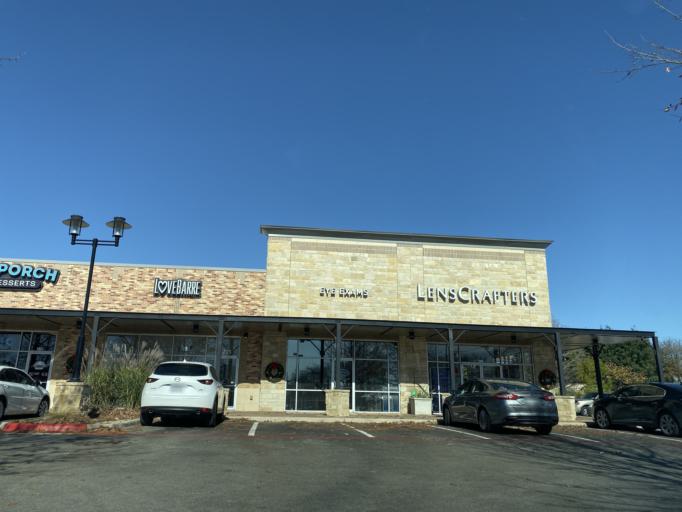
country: US
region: Texas
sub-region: Travis County
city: Windemere
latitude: 30.4774
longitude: -97.6713
